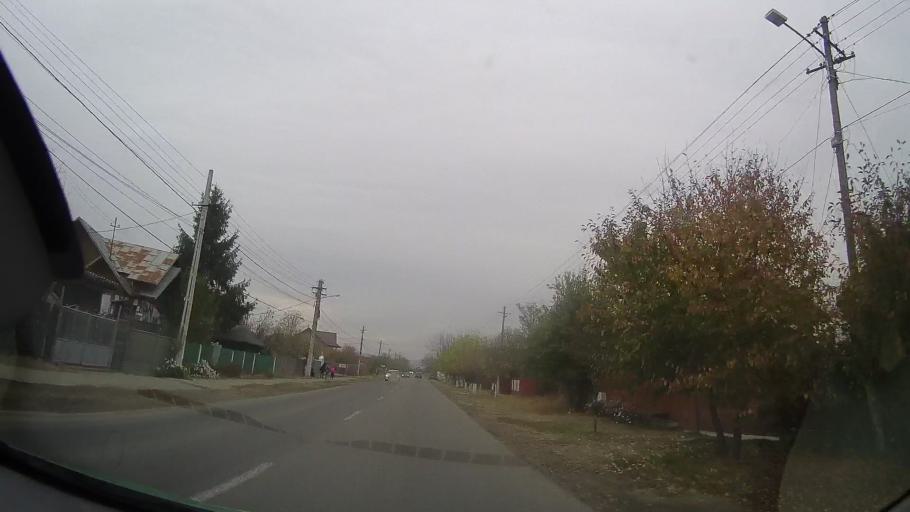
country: RO
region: Prahova
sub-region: Comuna Albesti-Paleologu
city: Albesti-Paleologu
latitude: 44.9565
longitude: 26.2308
